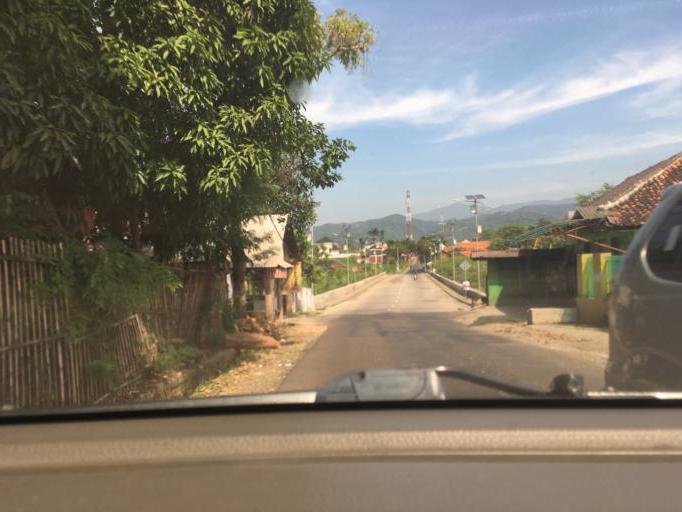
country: ID
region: West Java
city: Cilengkrang
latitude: -6.9453
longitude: 108.1011
